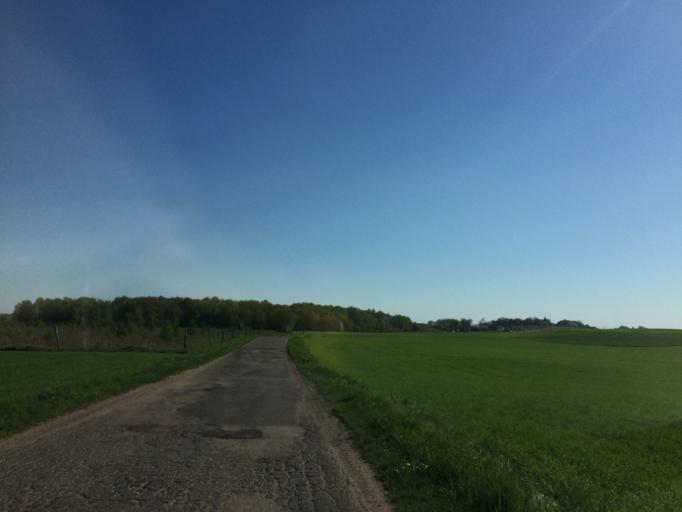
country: PL
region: Warmian-Masurian Voivodeship
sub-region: Powiat dzialdowski
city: Rybno
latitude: 53.4539
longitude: 19.9326
